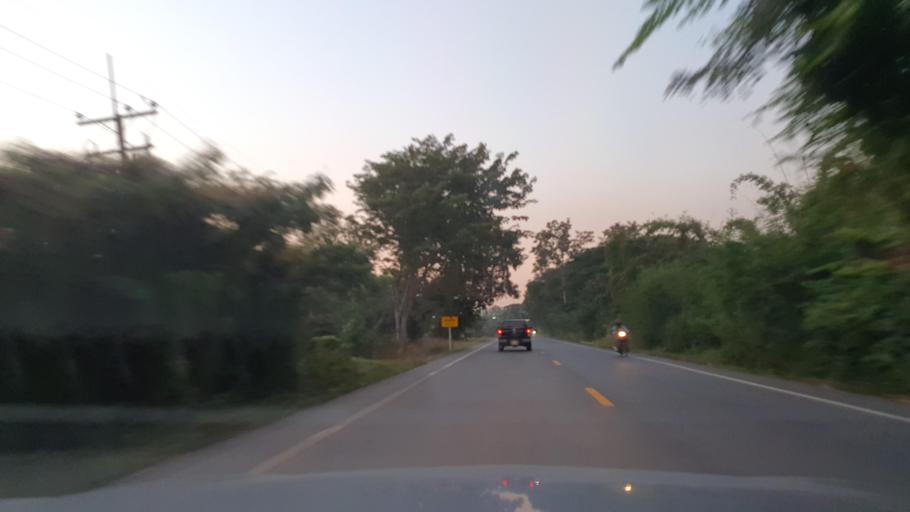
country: TH
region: Phayao
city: Dok Kham Tai
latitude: 19.1356
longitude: 100.0237
